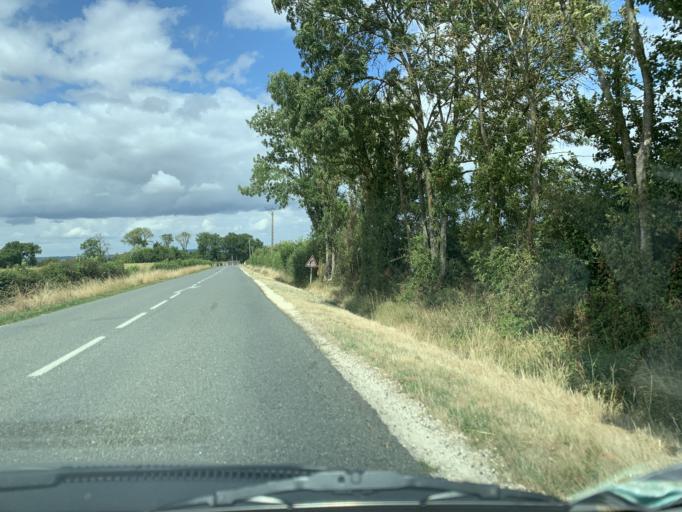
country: FR
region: Bourgogne
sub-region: Departement de la Nievre
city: Varzy
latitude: 47.3920
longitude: 3.4445
